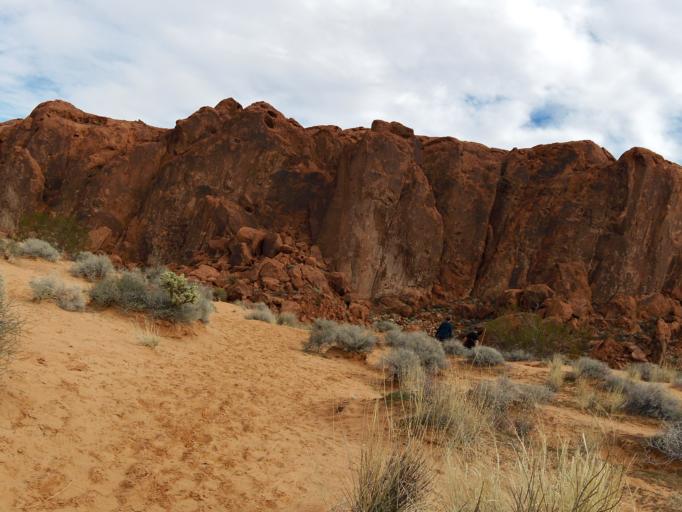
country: US
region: Nevada
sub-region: Clark County
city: Moapa Valley
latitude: 36.4888
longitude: -114.5272
